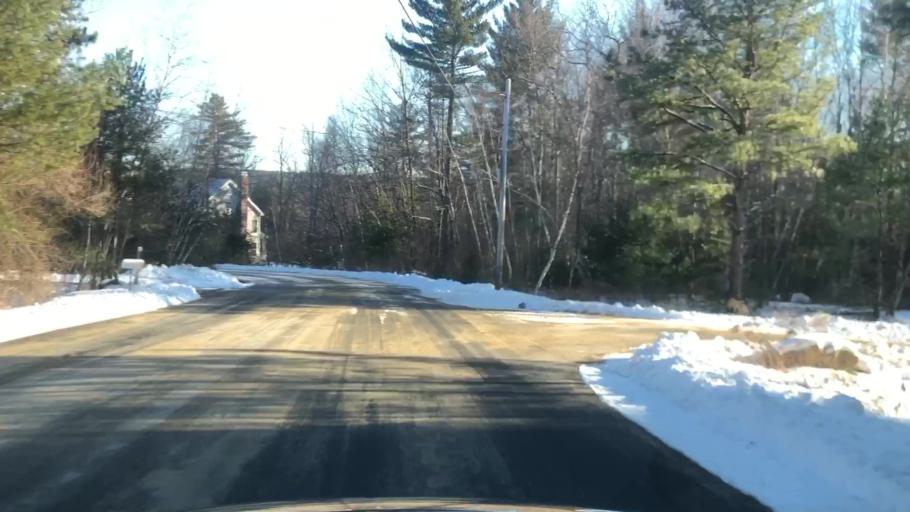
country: US
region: New Hampshire
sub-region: Hillsborough County
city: Milford
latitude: 42.8003
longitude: -71.6687
